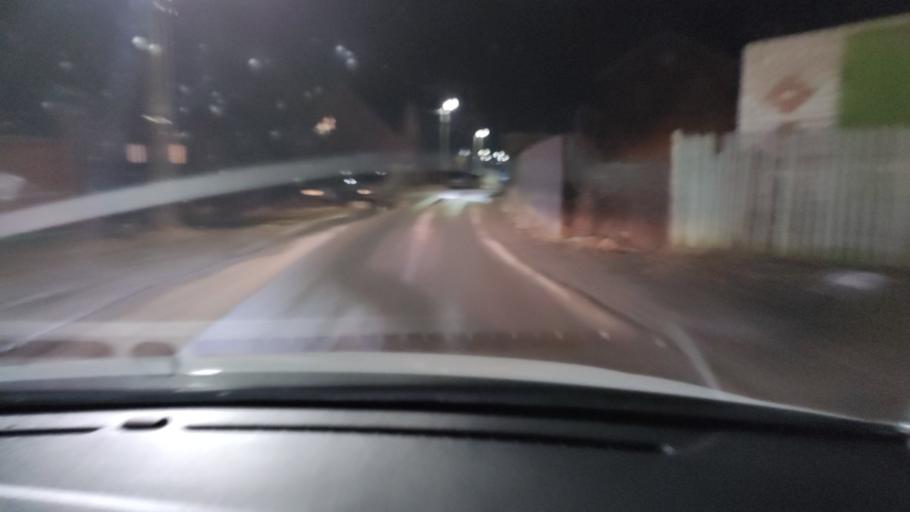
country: RU
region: Tatarstan
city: Vysokaya Gora
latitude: 55.8534
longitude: 49.2368
